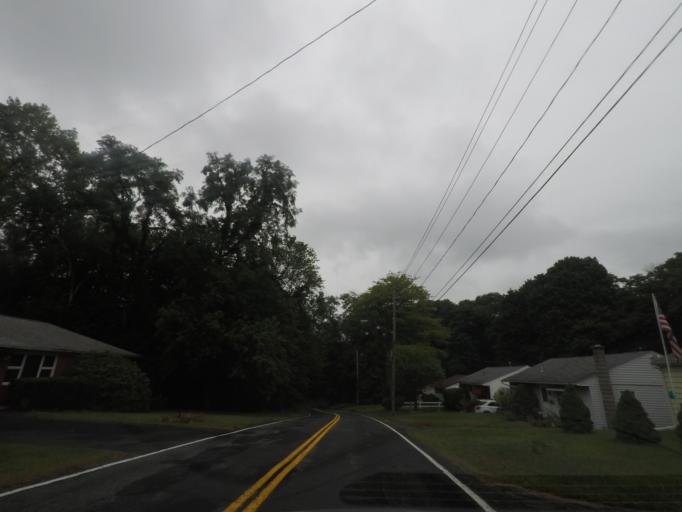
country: US
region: New York
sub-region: Rensselaer County
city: Hampton Manor
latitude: 42.6202
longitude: -73.7185
